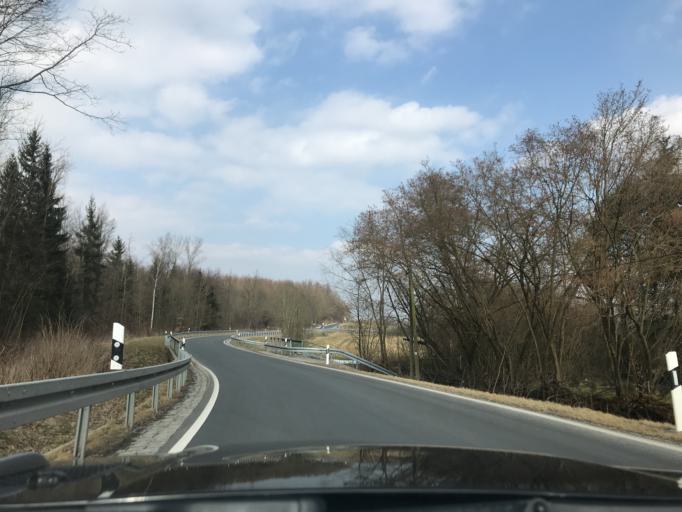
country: DE
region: Thuringia
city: Oberdorla
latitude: 51.1792
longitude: 10.3998
